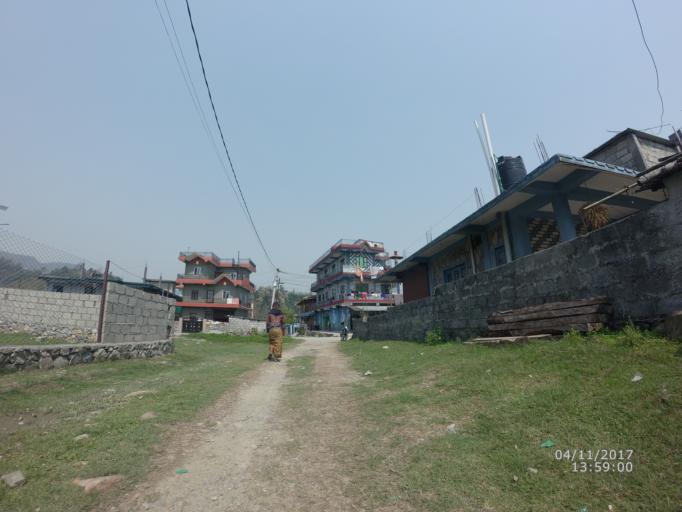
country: NP
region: Western Region
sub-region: Gandaki Zone
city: Pokhara
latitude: 28.1870
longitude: 84.0429
